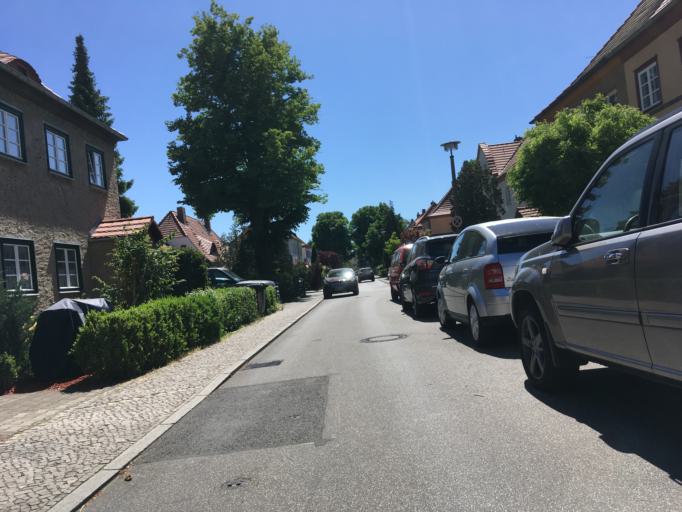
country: DE
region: Berlin
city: Johannisthal
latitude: 52.4510
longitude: 13.5064
